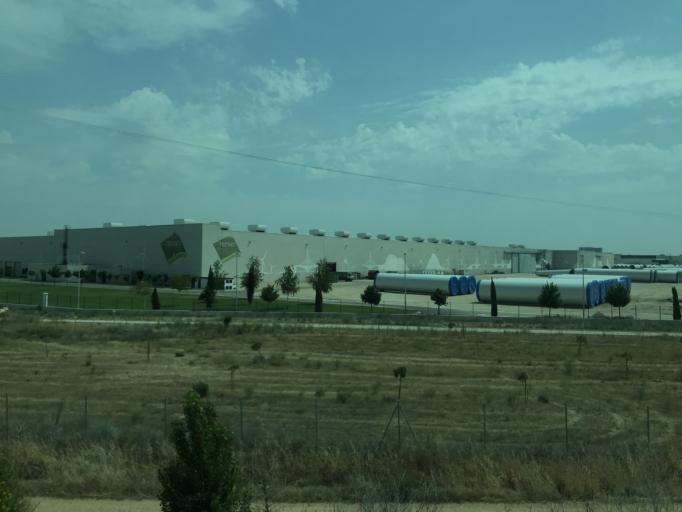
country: ES
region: Castille and Leon
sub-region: Provincia de Burgos
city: Villalba de Duero
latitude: 41.6594
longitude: -3.7265
